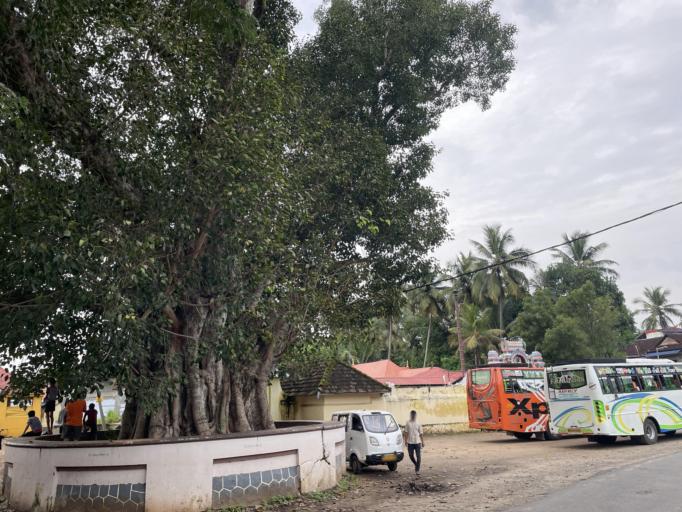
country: IN
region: Kerala
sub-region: Palakkad district
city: Chittur
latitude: 10.6929
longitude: 76.7419
